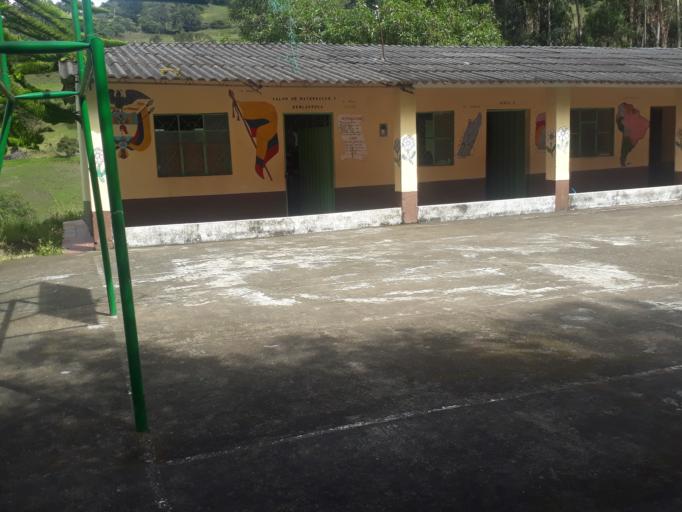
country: CO
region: Boyaca
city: El Espino
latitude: 6.4951
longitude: -72.4873
